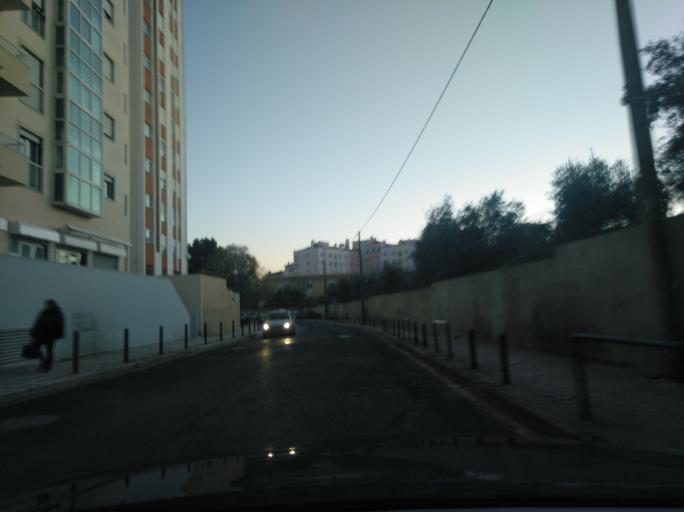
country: PT
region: Lisbon
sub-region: Odivelas
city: Olival do Basto
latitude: 38.7781
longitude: -9.1600
